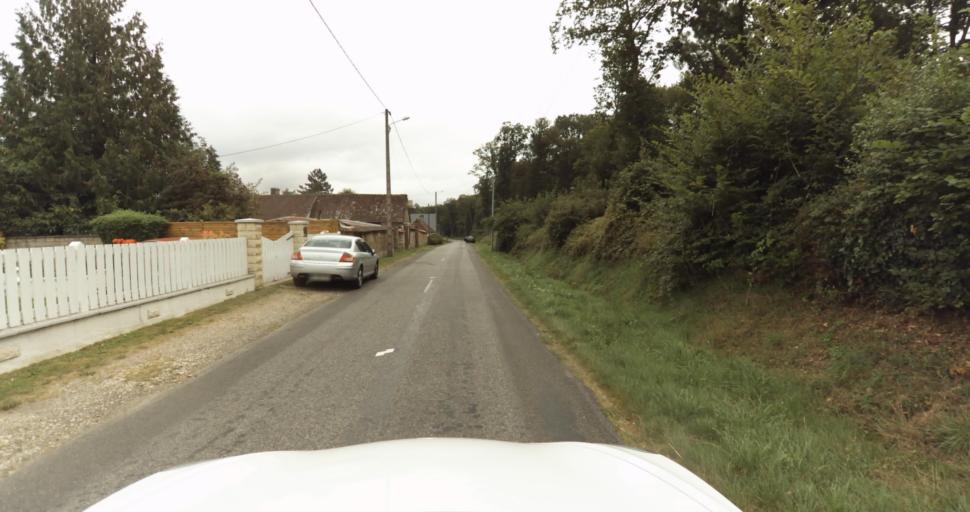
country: FR
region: Haute-Normandie
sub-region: Departement de l'Eure
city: Arnieres-sur-Iton
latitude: 48.9539
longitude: 1.0676
